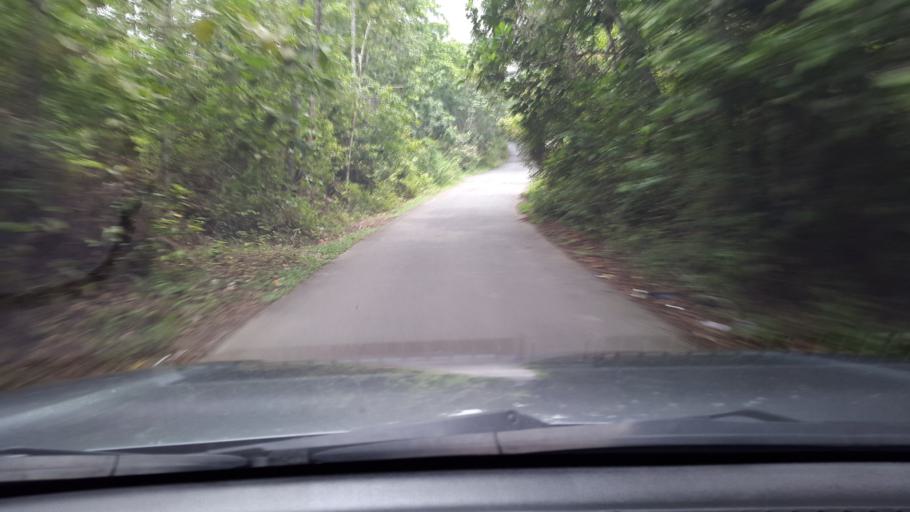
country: ID
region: South Sumatra
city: Gunungmenang
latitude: -3.1041
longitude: 103.8346
